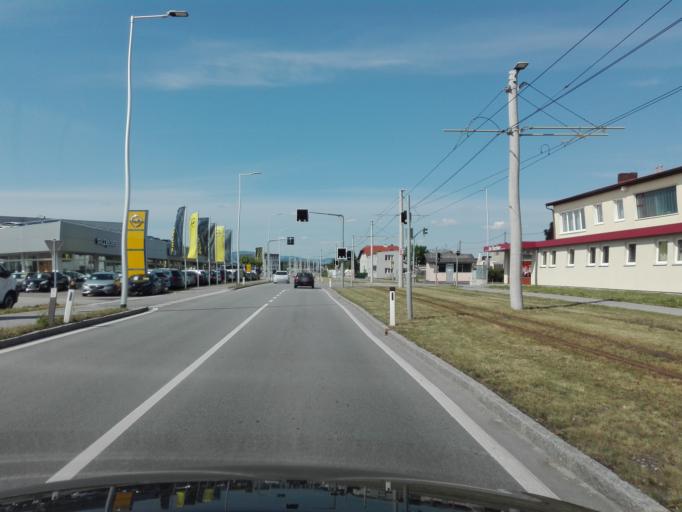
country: AT
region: Upper Austria
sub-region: Politischer Bezirk Linz-Land
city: Traun
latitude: 48.2304
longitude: 14.2339
